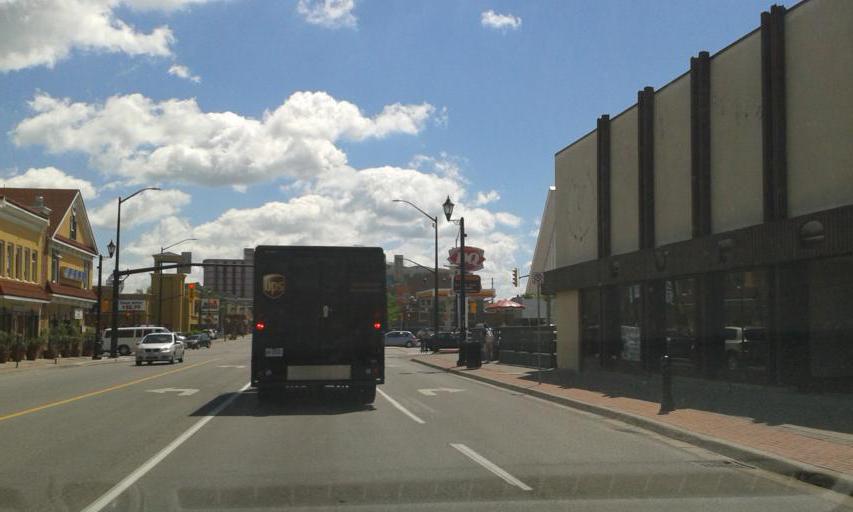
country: CA
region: Ontario
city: Niagara Falls
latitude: 43.0895
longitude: -79.0858
